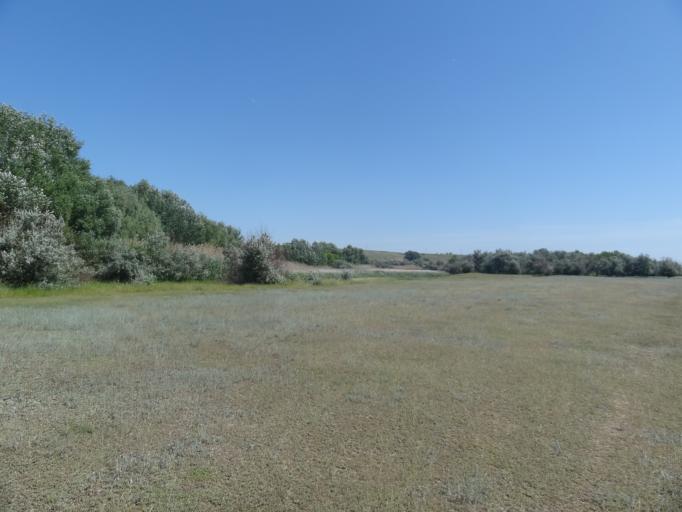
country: RU
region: Saratov
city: Krasnoarmeysk
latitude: 51.1542
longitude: 45.9256
